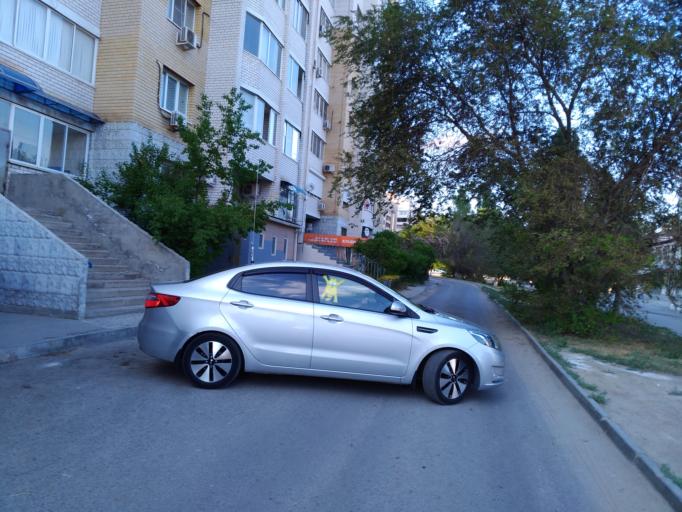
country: RU
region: Volgograd
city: Volgograd
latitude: 48.7202
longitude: 44.5115
